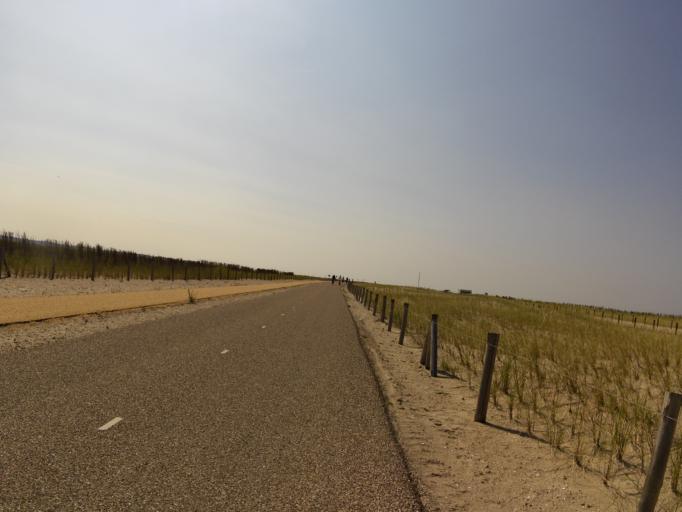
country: NL
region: North Holland
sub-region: Gemeente Schagen
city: Harenkarspel
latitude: 52.7708
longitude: 4.6571
